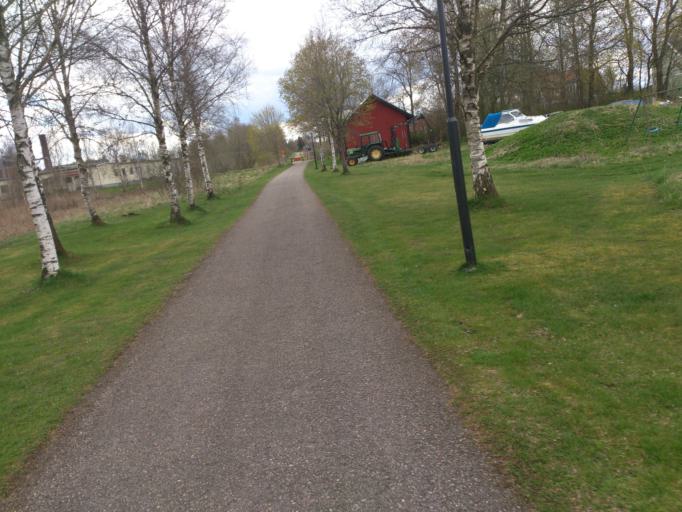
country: SE
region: Vaestra Goetaland
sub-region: Falkopings Kommun
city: Falkoeping
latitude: 57.9861
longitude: 13.5302
